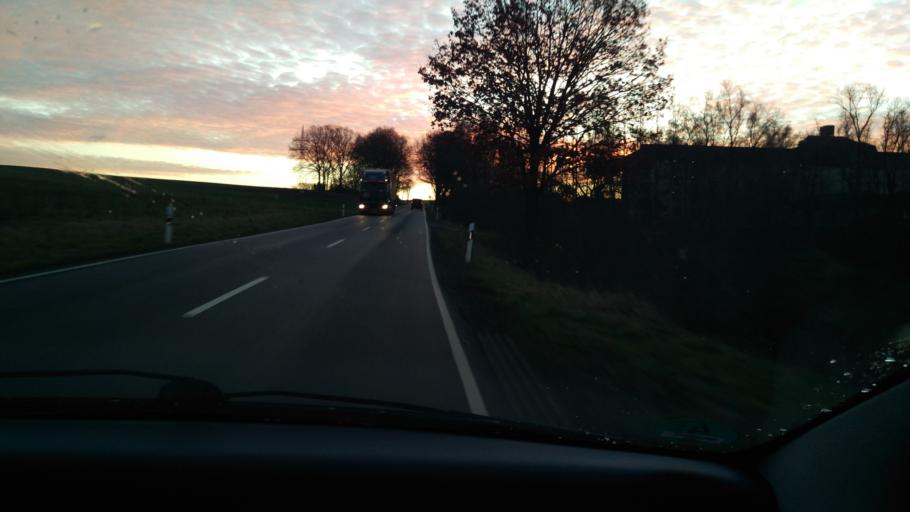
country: DE
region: Hesse
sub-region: Regierungsbezirk Giessen
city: Homberg
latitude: 50.7385
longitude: 9.0110
